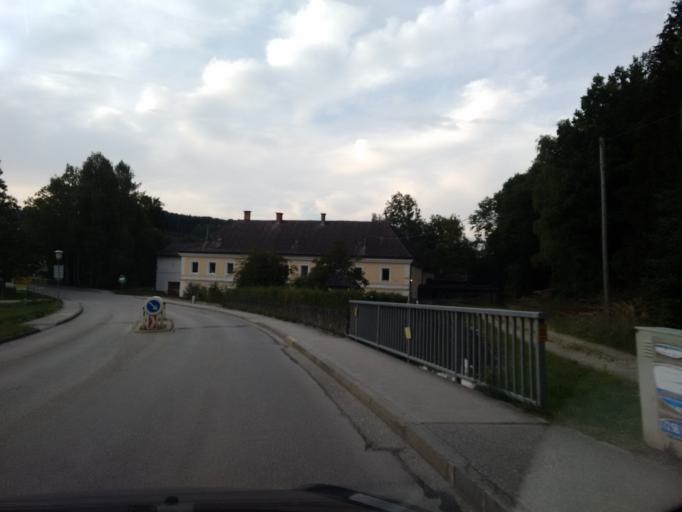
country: AT
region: Upper Austria
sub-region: Politischer Bezirk Steyr-Land
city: Bad Hall
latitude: 48.0377
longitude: 14.2025
